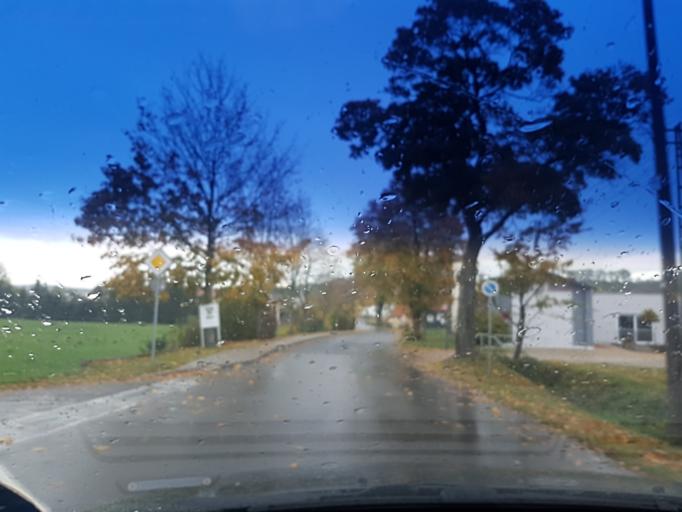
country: DE
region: Bavaria
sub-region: Regierungsbezirk Mittelfranken
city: Burghaslach
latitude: 49.7619
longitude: 10.5711
